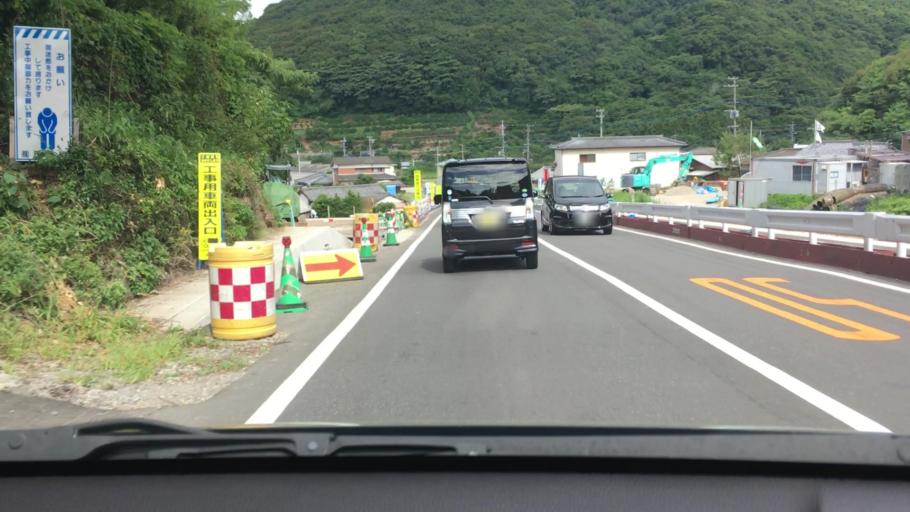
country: JP
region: Nagasaki
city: Togitsu
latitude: 32.8599
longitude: 129.8047
